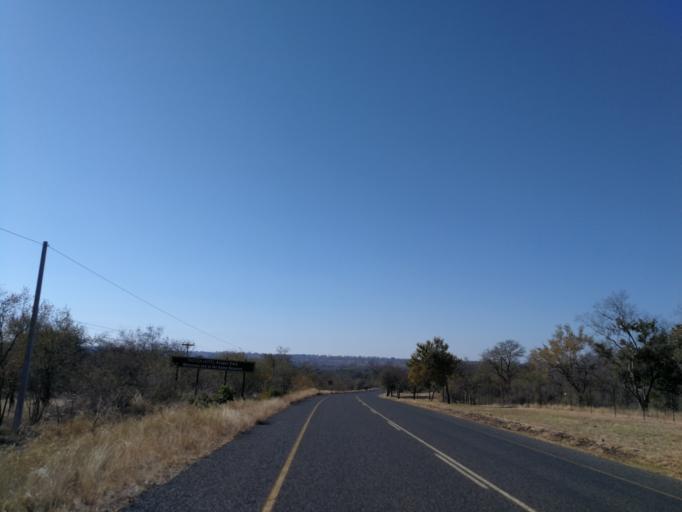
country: ZA
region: Limpopo
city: Thulamahashi
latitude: -24.9762
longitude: 31.4754
